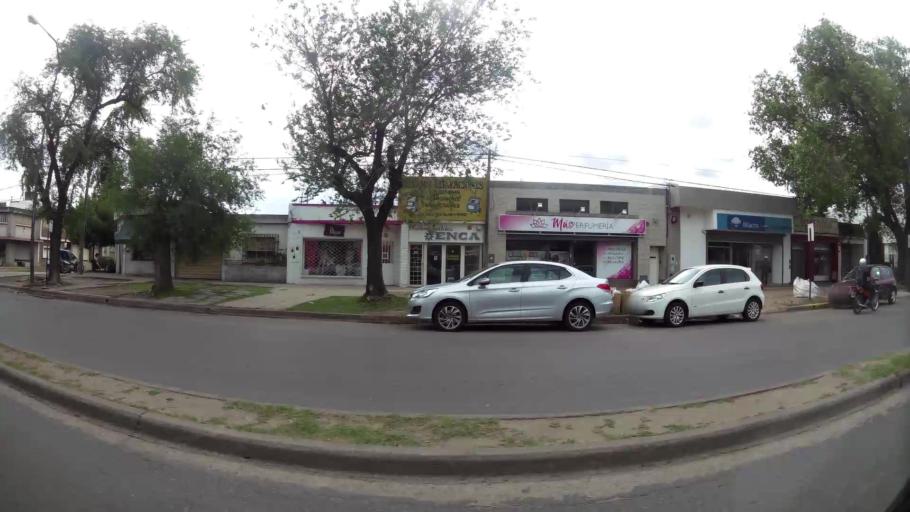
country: AR
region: Santa Fe
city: Gobernador Galvez
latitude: -33.0026
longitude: -60.6761
